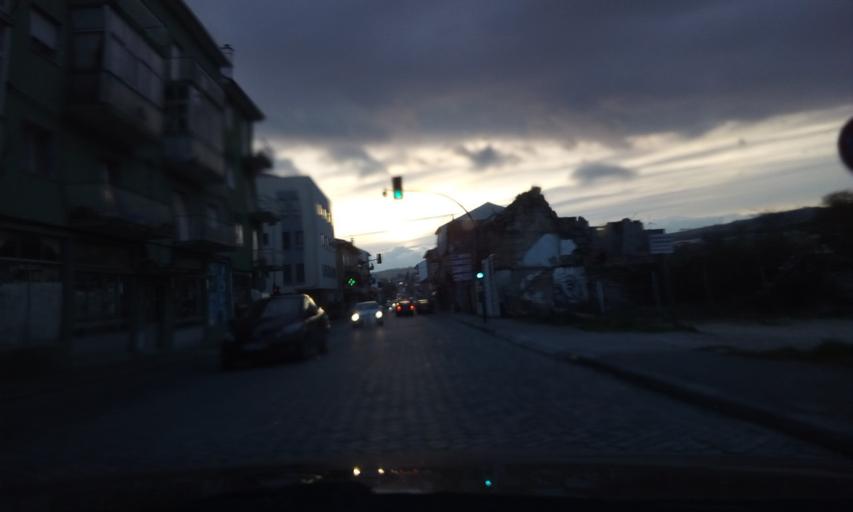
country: PT
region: Guarda
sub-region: Guarda
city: Sequeira
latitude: 40.5562
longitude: -7.2392
